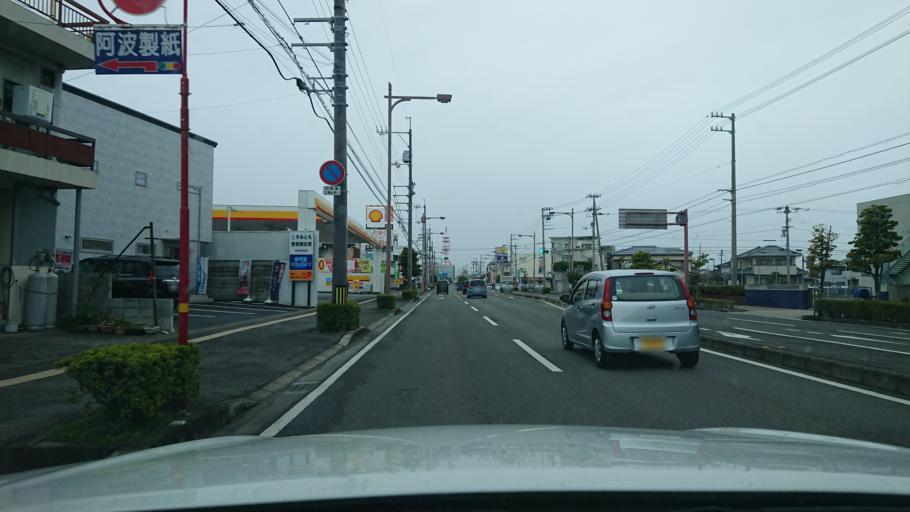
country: JP
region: Tokushima
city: Tokushima-shi
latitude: 34.0853
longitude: 134.5252
